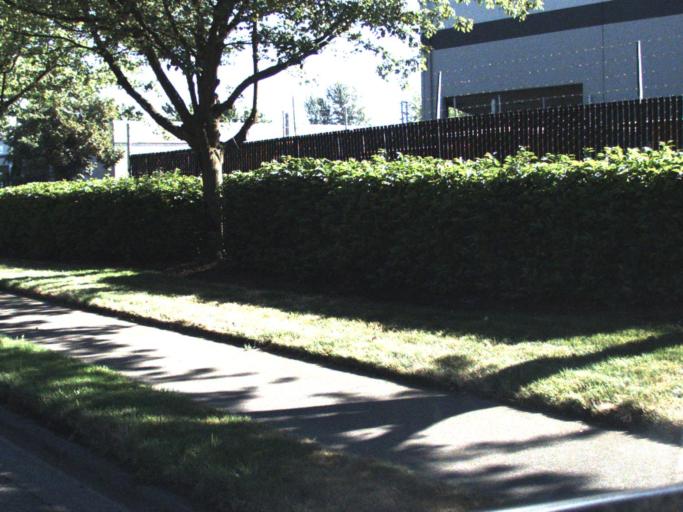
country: US
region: Washington
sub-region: King County
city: Kent
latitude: 47.4004
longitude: -122.2493
